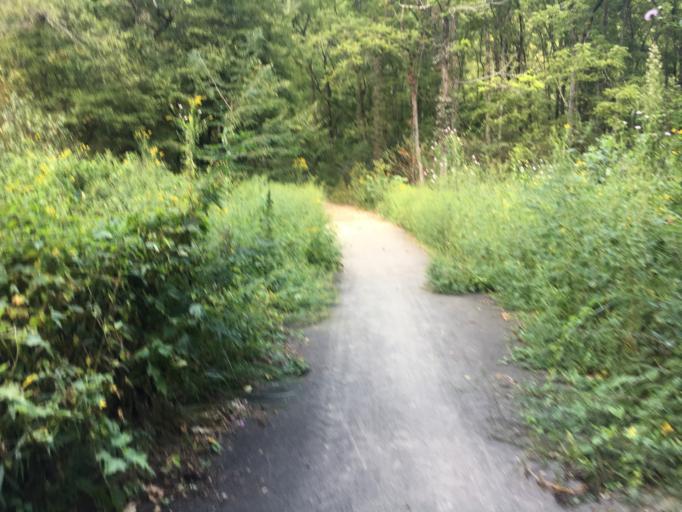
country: US
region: North Carolina
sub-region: Graham County
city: Robbinsville
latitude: 35.2746
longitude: -83.6793
